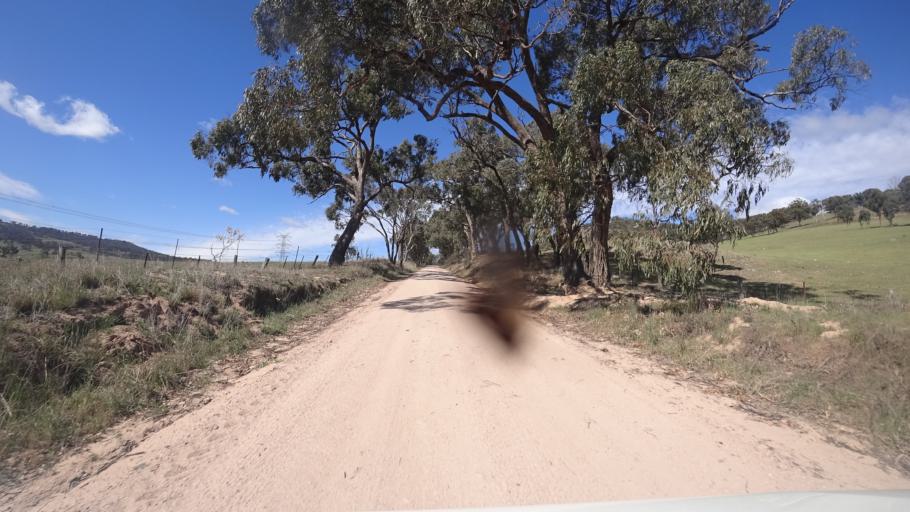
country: AU
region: New South Wales
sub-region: Lithgow
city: Portland
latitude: -33.5244
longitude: 149.9355
